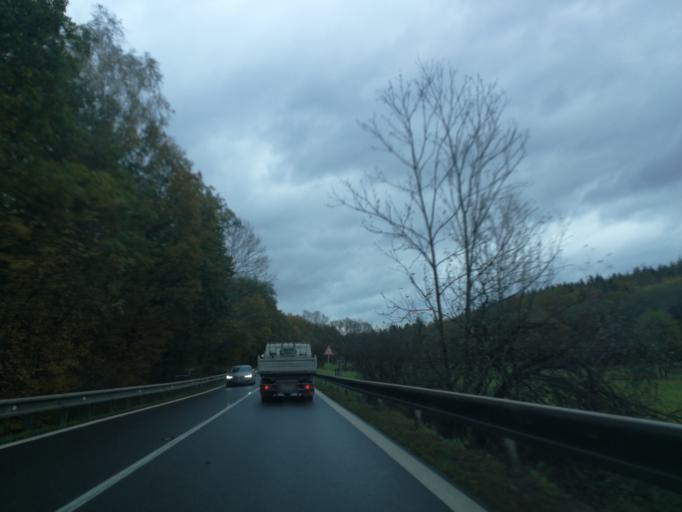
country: CZ
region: Zlin
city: Valasske Mezirici
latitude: 49.5048
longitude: 17.9957
